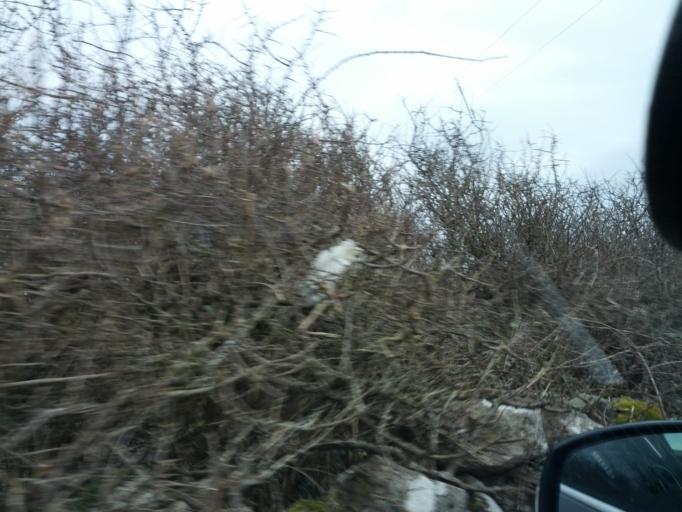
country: IE
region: Connaught
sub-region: County Galway
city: Oranmore
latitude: 53.2047
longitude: -8.9235
